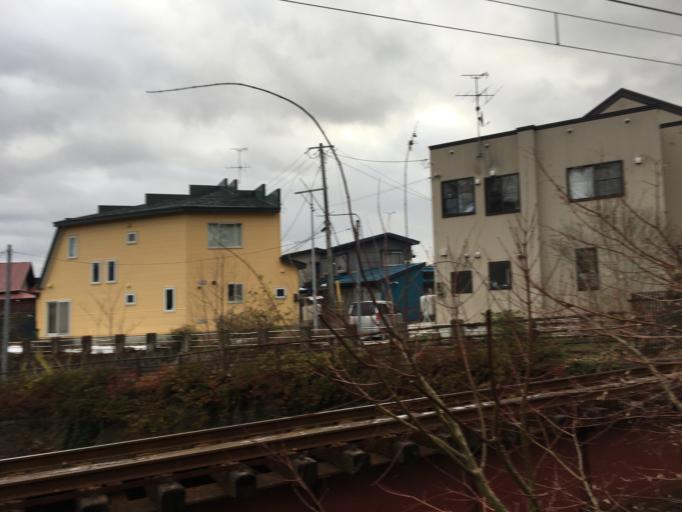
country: JP
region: Aomori
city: Hirosaki
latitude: 40.5941
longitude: 140.4683
